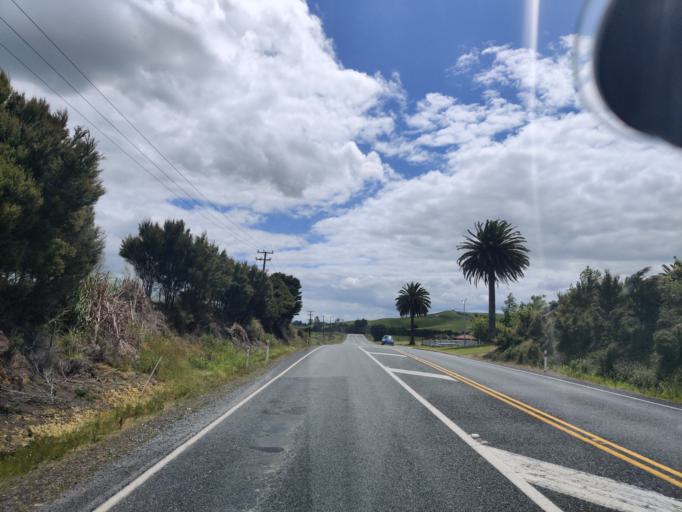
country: NZ
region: Northland
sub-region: Far North District
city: Paihia
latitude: -35.2811
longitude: 174.0449
